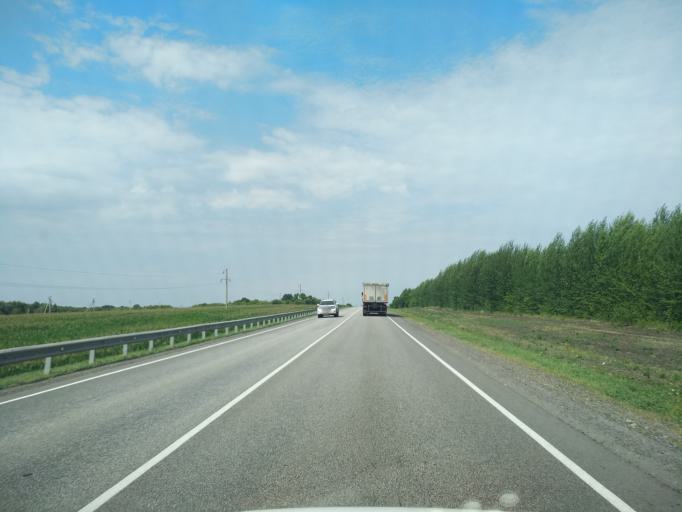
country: RU
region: Voronezj
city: Orlovo
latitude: 51.6761
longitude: 39.7192
